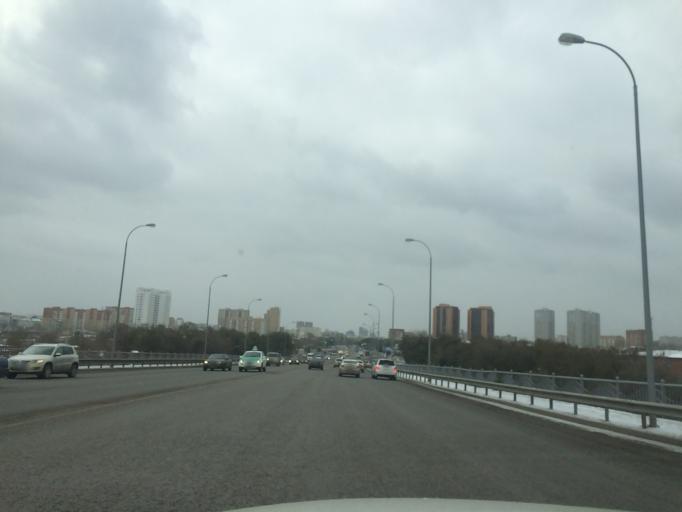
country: KZ
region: Astana Qalasy
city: Astana
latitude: 51.1706
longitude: 71.4803
